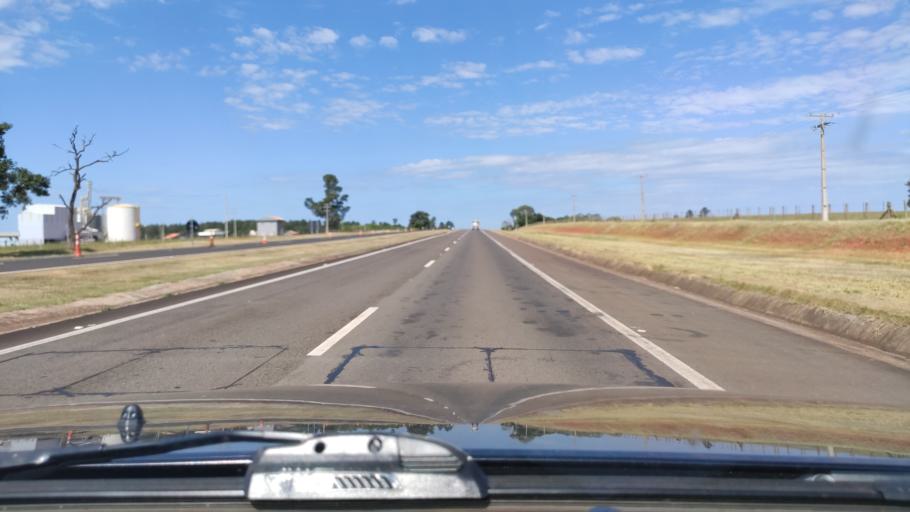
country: BR
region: Sao Paulo
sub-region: Rancharia
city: Rancharia
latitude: -22.4525
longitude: -50.9790
